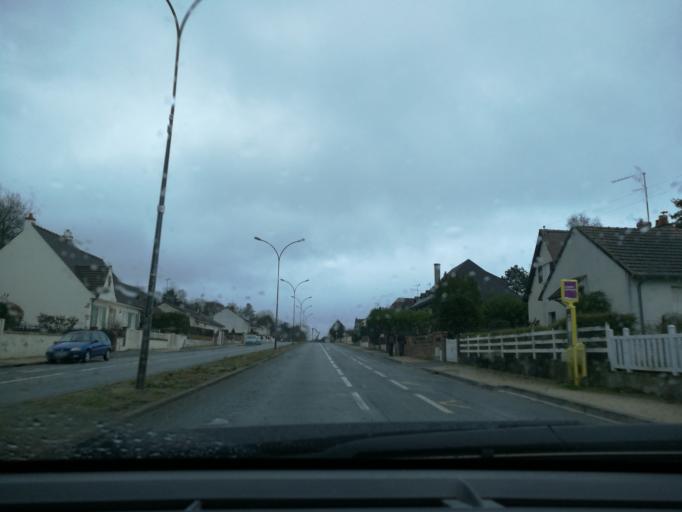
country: FR
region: Centre
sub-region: Departement du Loiret
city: Fleury-les-Aubrais
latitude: 47.9331
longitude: 1.9256
